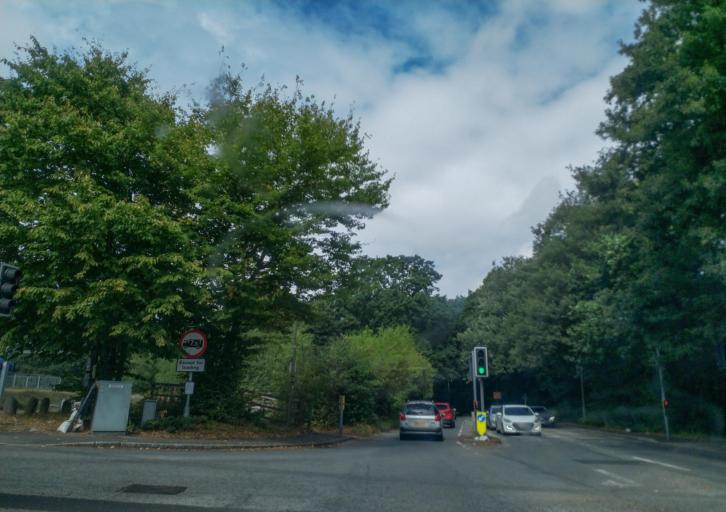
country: GB
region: England
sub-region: Bracknell Forest
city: Sandhurst
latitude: 51.3269
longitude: -0.7778
